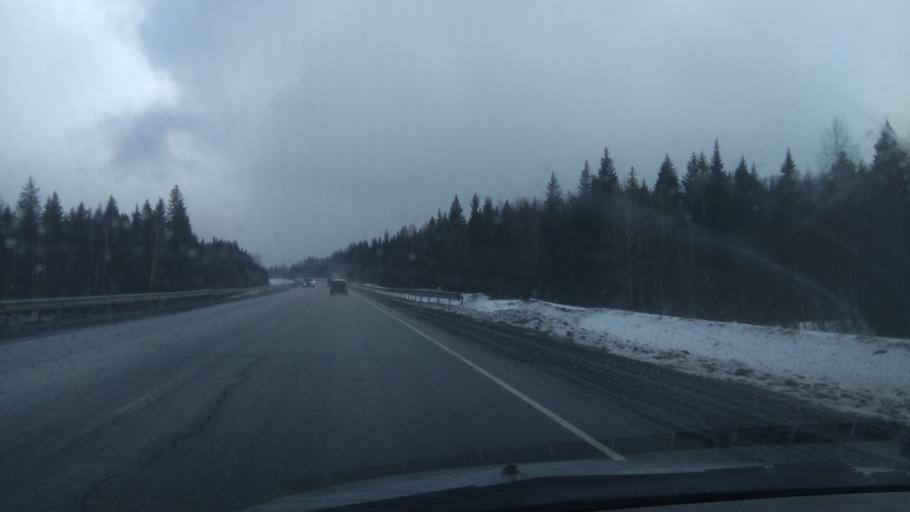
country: RU
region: Sverdlovsk
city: Arti
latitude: 56.7885
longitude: 58.5069
